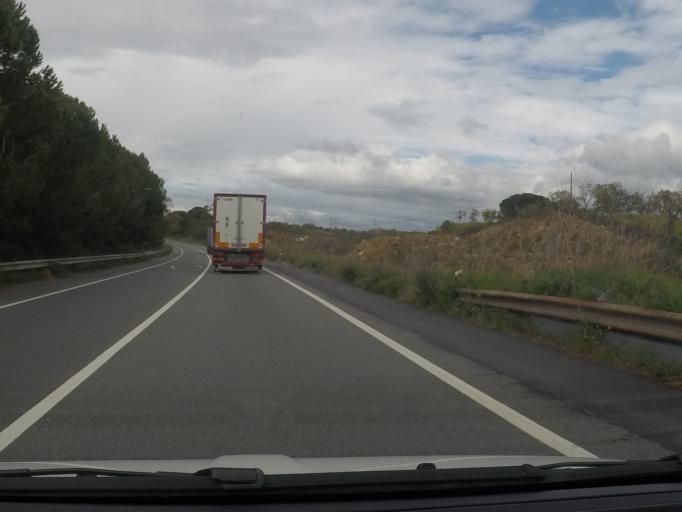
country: PT
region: Setubal
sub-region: Santiago do Cacem
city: Santiago do Cacem
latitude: 38.0772
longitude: -8.6437
